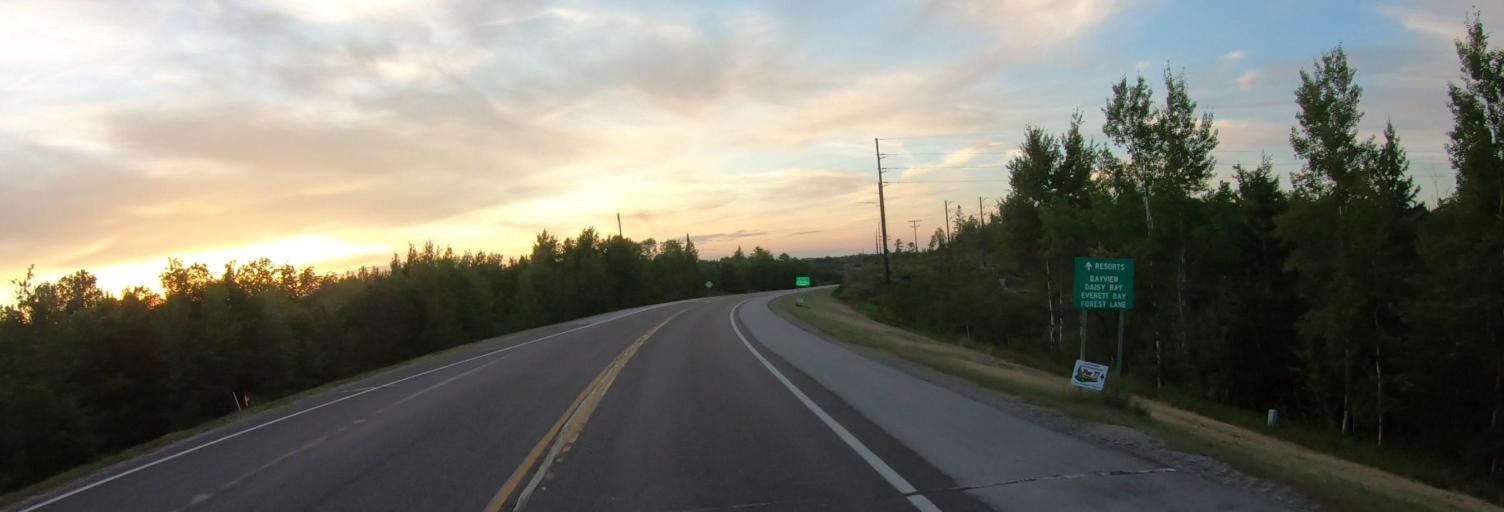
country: US
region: Minnesota
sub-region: Saint Louis County
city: Aurora
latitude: 47.7858
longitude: -92.3642
